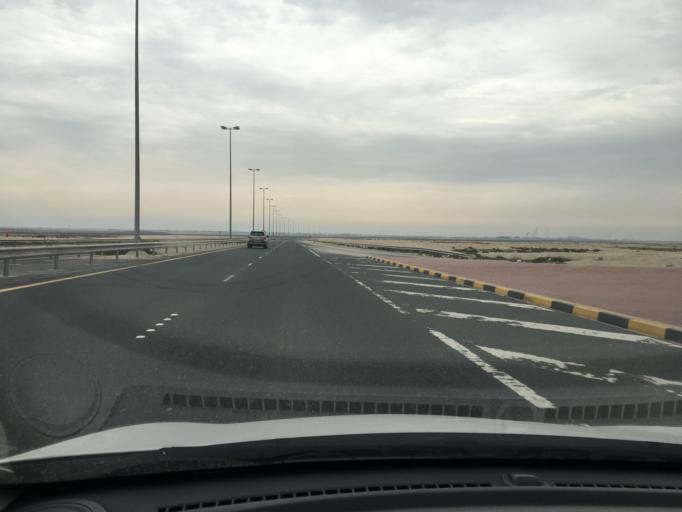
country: BH
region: Central Governorate
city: Dar Kulayb
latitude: 25.8726
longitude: 50.5800
